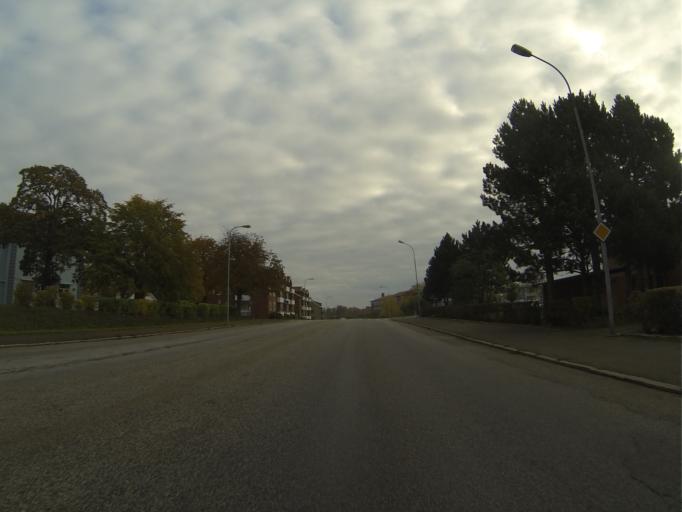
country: SE
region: Skane
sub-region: Tomelilla Kommun
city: Tomelilla
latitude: 55.5412
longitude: 13.9468
